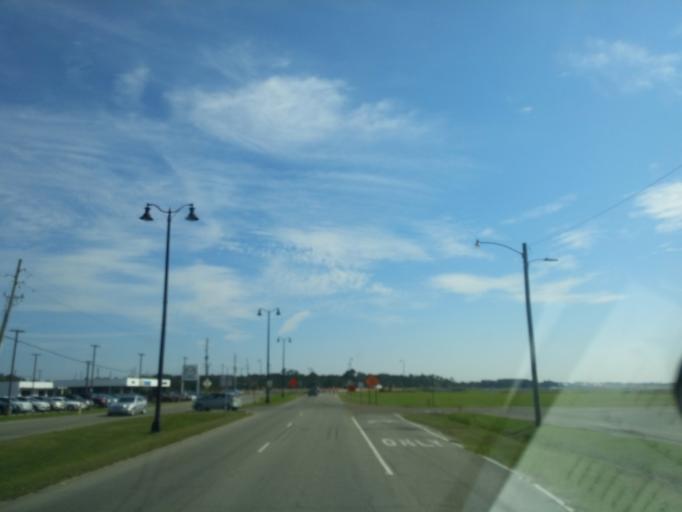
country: US
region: Mississippi
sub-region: Harrison County
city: West Gulfport
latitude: 30.4199
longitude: -89.0913
